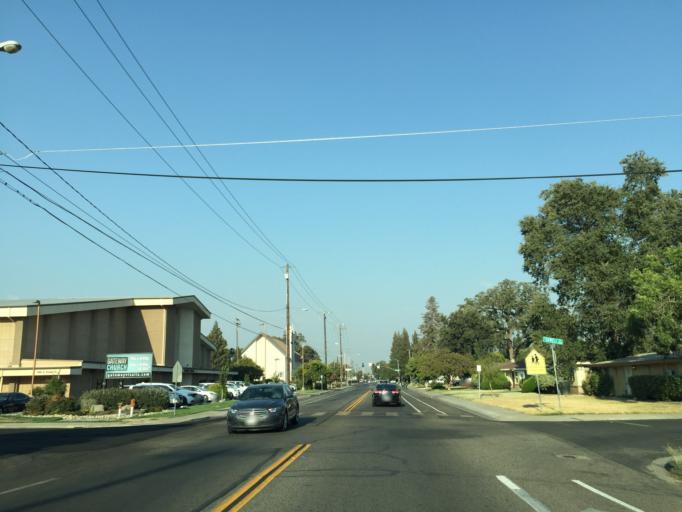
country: US
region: California
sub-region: Tulare County
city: Visalia
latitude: 36.3200
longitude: -119.3035
